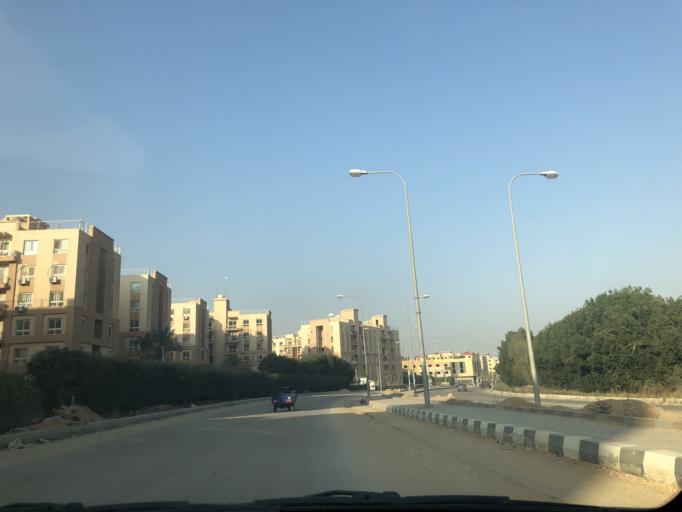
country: EG
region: Al Jizah
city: Madinat Sittah Uktubar
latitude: 29.9097
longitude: 31.0575
